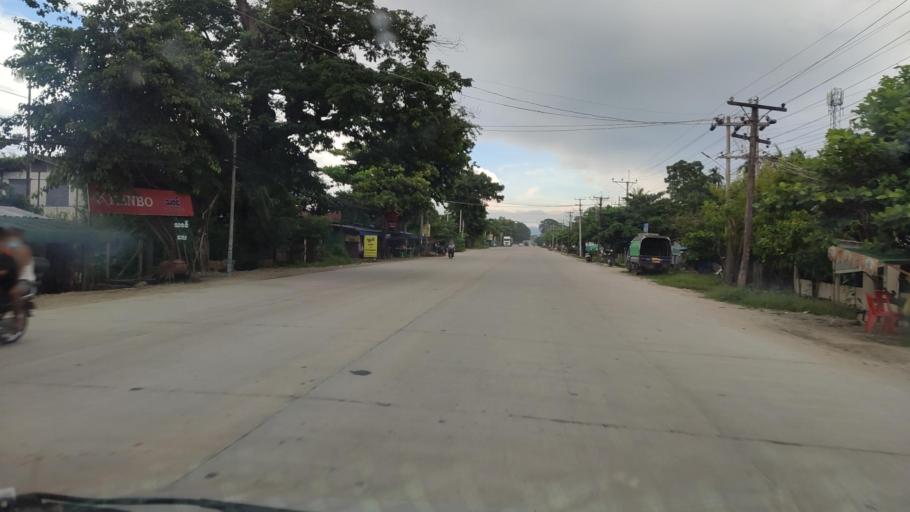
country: MM
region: Bago
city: Taungoo
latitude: 18.9039
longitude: 96.4357
